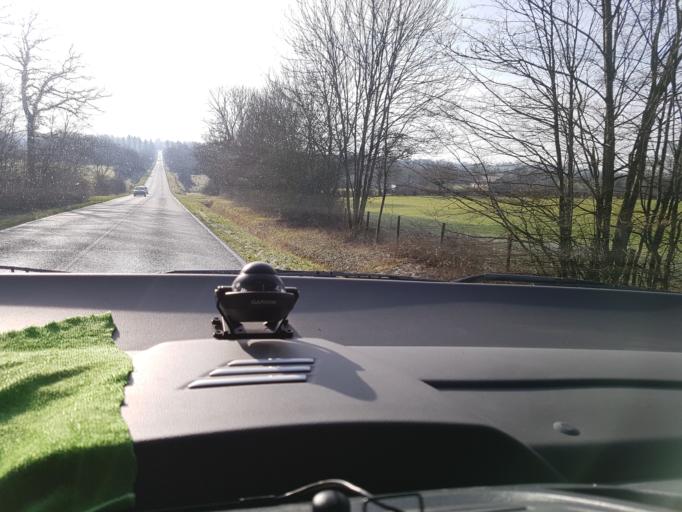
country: FR
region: Nord-Pas-de-Calais
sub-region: Departement du Nord
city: Wignehies
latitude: 50.0481
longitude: 4.0269
